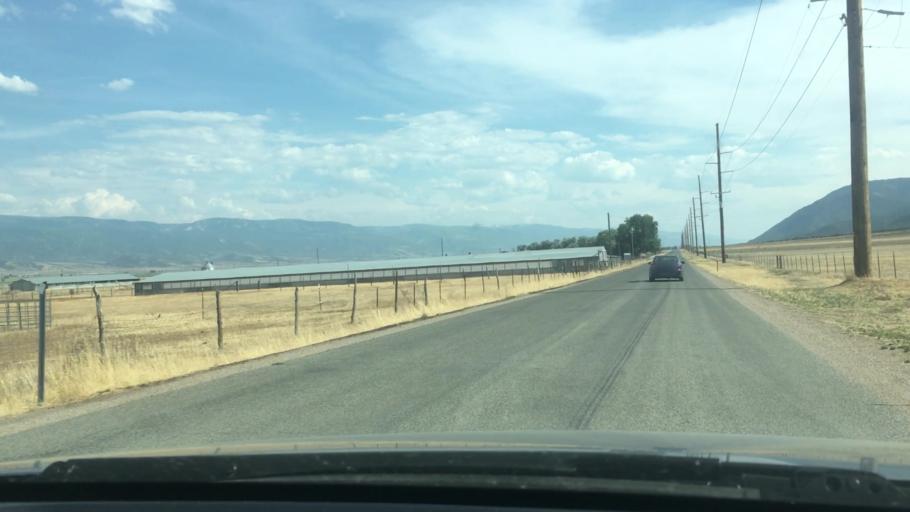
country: US
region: Utah
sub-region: Sanpete County
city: Moroni
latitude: 39.5299
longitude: -111.6398
